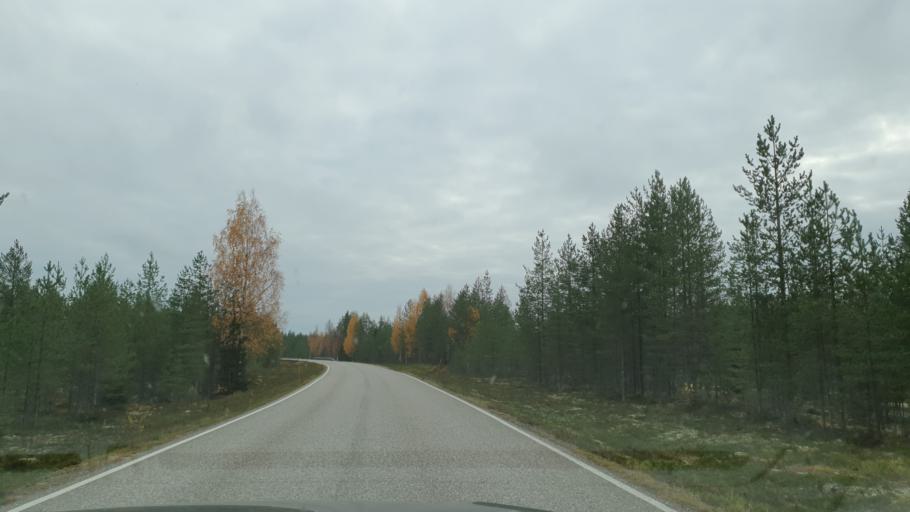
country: FI
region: Kainuu
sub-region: Kajaani
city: Paltamo
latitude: 64.6471
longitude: 27.9656
